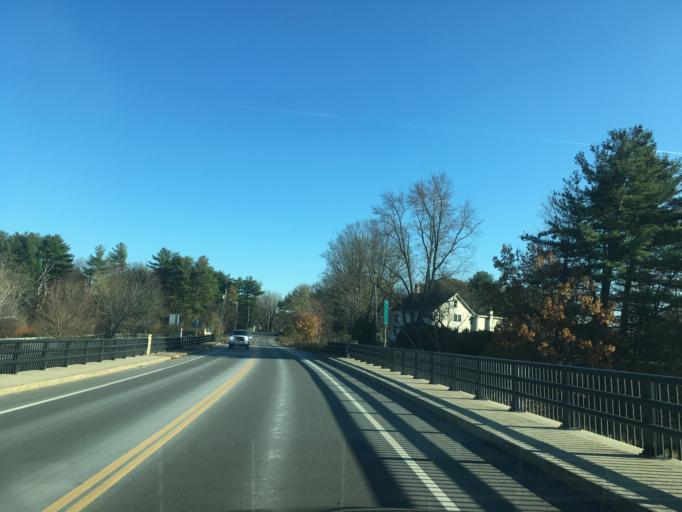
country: US
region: New Hampshire
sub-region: Rockingham County
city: Stratham Station
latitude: 43.0395
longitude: -70.9280
